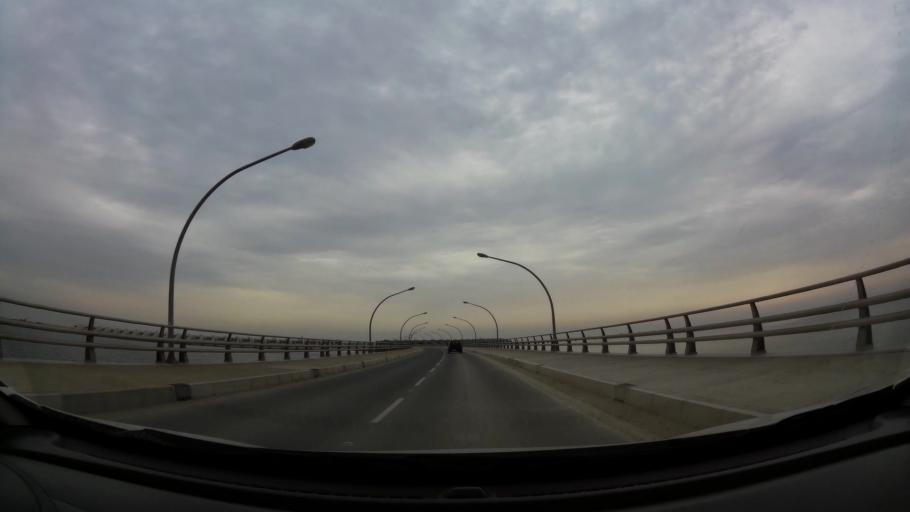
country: BH
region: Central Governorate
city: Dar Kulayb
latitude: 25.8289
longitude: 50.5980
